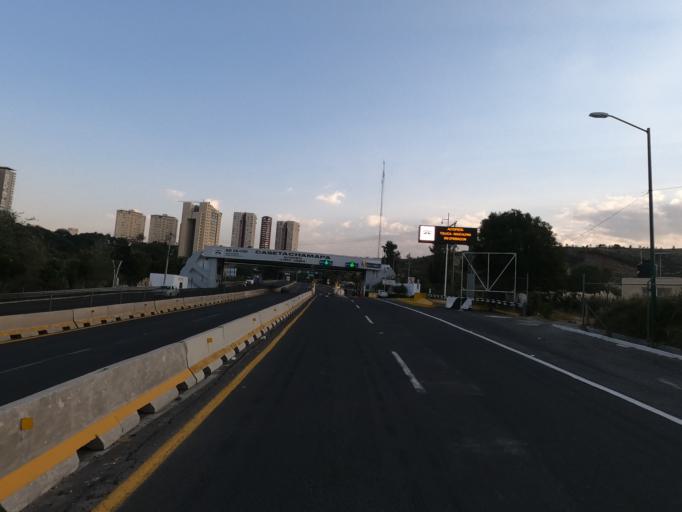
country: MX
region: Mexico
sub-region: Naucalpan de Juarez
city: Ejido el Castillo
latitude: 19.4325
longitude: -99.2971
